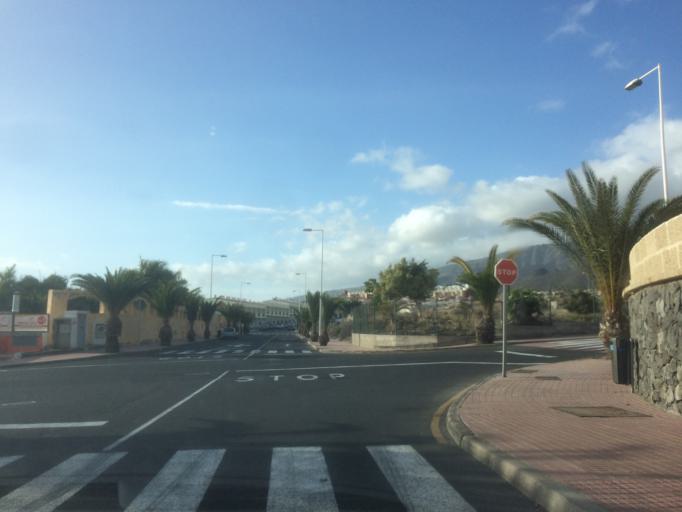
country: ES
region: Canary Islands
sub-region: Provincia de Santa Cruz de Tenerife
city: Playa de las Americas
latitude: 28.0899
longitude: -16.7274
